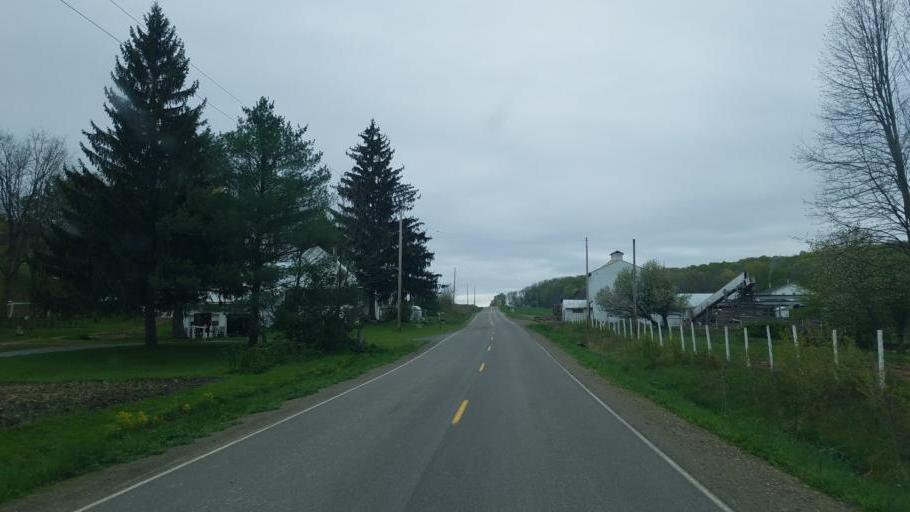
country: US
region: Pennsylvania
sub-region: Tioga County
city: Westfield
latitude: 42.0451
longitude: -77.4664
